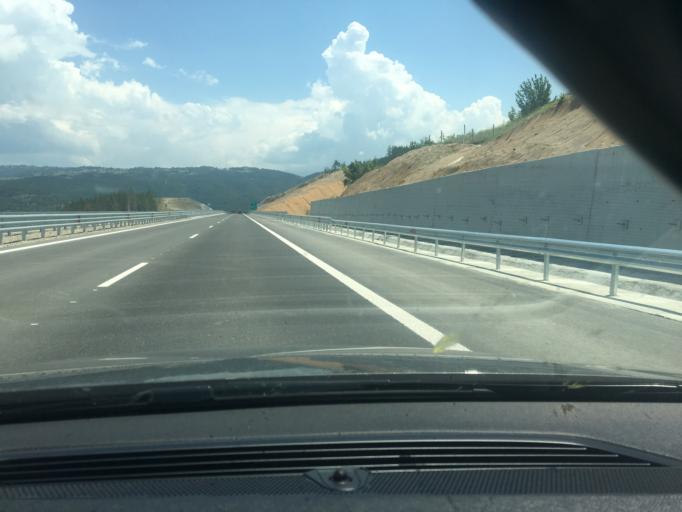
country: BG
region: Blagoevgrad
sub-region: Obshtina Blagoevgrad
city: Blagoevgrad
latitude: 41.9725
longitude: 23.0800
